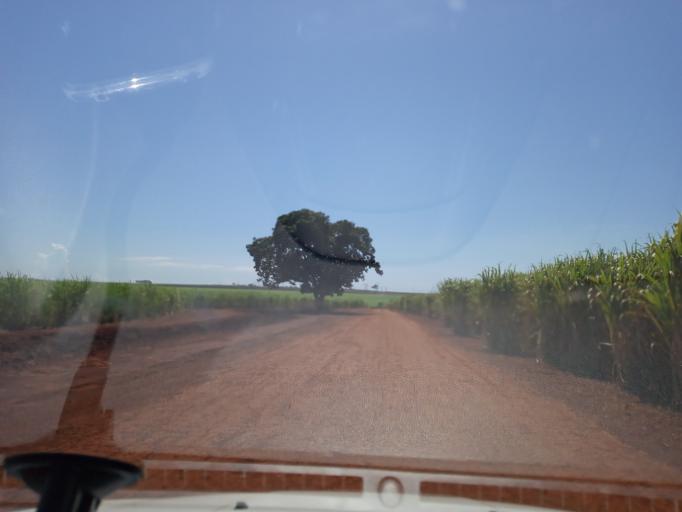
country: BR
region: Goias
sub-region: Itumbiara
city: Itumbiara
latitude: -18.4423
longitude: -49.1485
